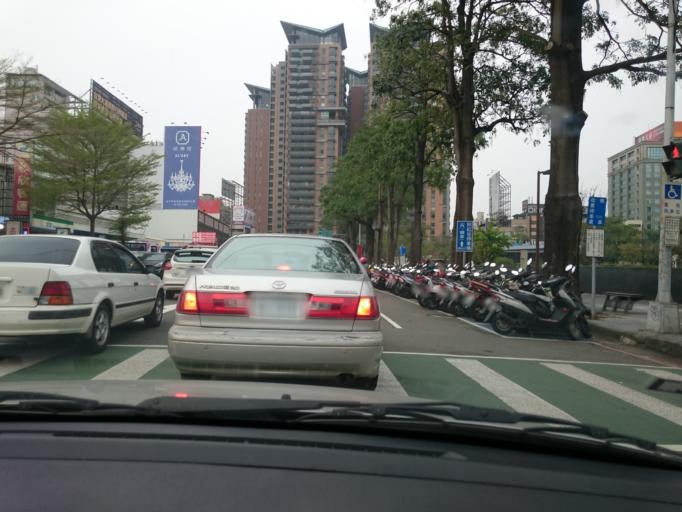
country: TW
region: Taiwan
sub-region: Taichung City
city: Taichung
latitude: 24.1678
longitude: 120.6384
